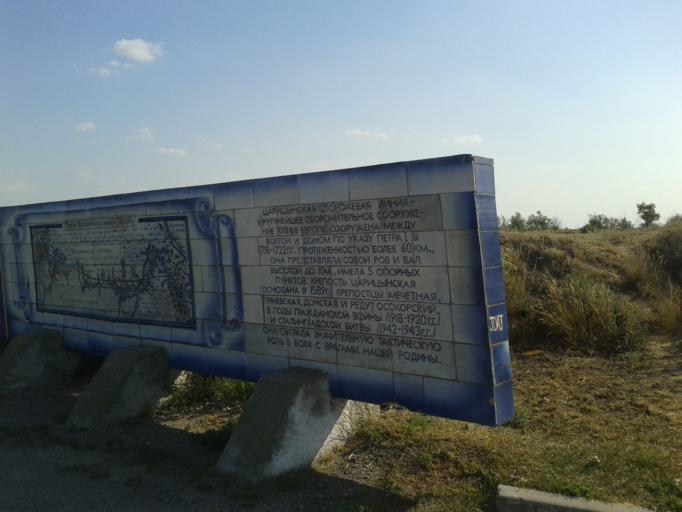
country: RU
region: Volgograd
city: Ilovlya
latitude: 49.0472
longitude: 44.1339
